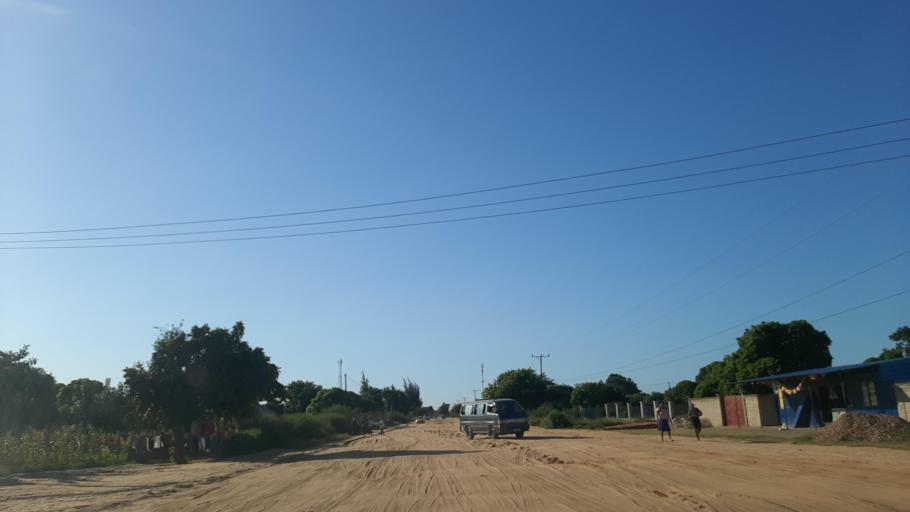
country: MZ
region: Maputo City
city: Maputo
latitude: -25.7445
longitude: 32.5434
